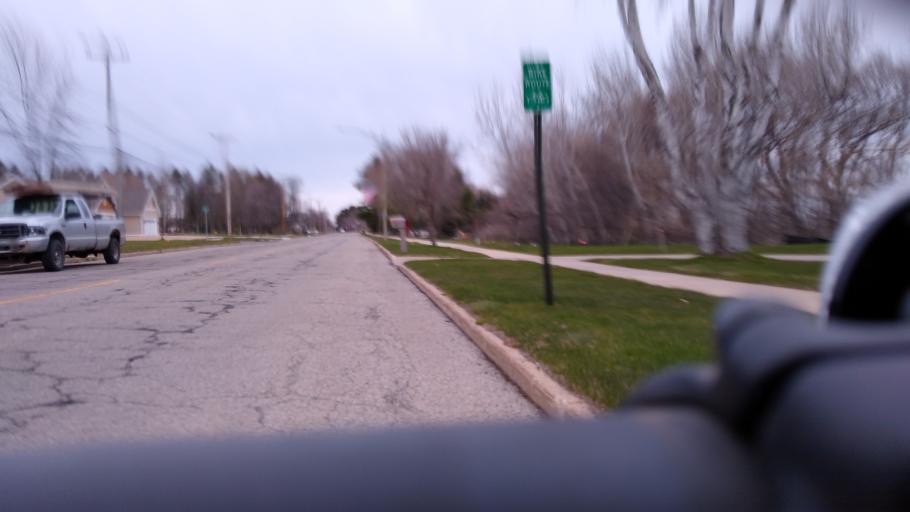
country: US
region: Michigan
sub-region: Delta County
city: Escanaba
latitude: 45.7210
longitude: -87.0702
